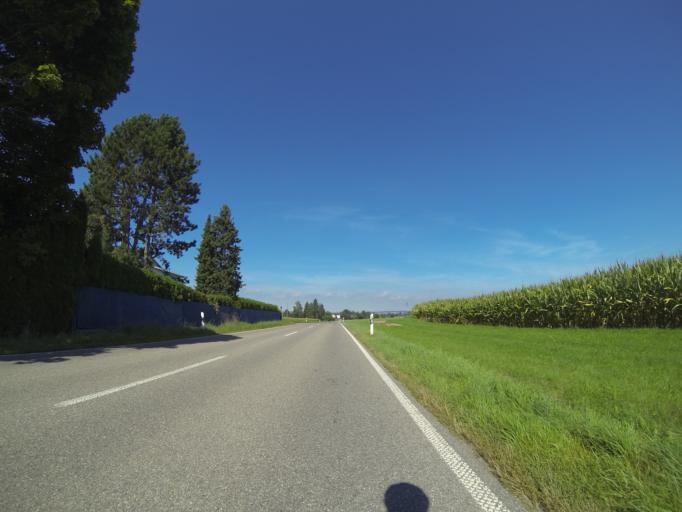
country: DE
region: Baden-Wuerttemberg
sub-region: Tuebingen Region
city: Erbach
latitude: 48.3031
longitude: 9.9081
